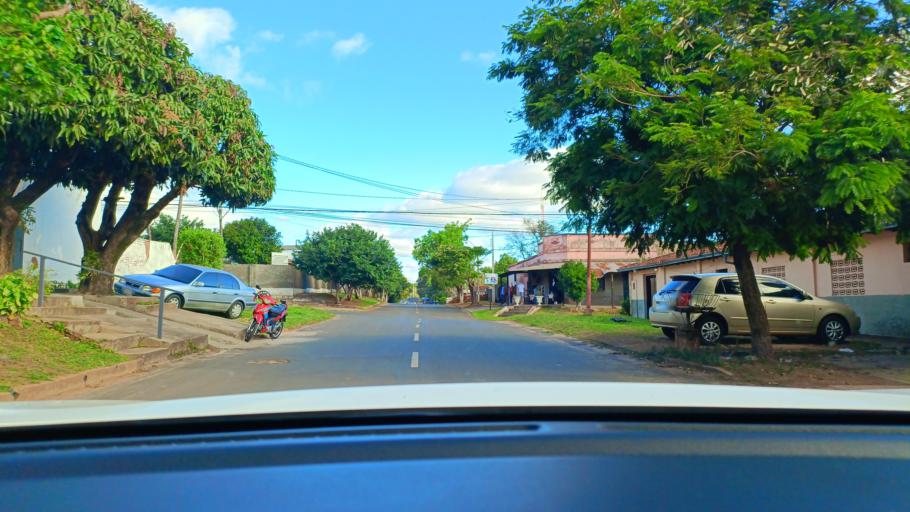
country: PY
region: San Pedro
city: Guayaybi
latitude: -24.6687
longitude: -56.4432
